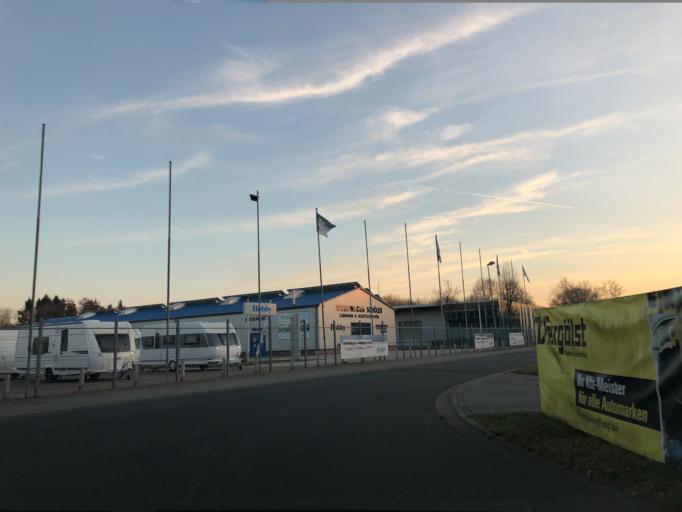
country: DE
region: Lower Saxony
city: Papenburg
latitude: 53.0960
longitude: 7.4064
